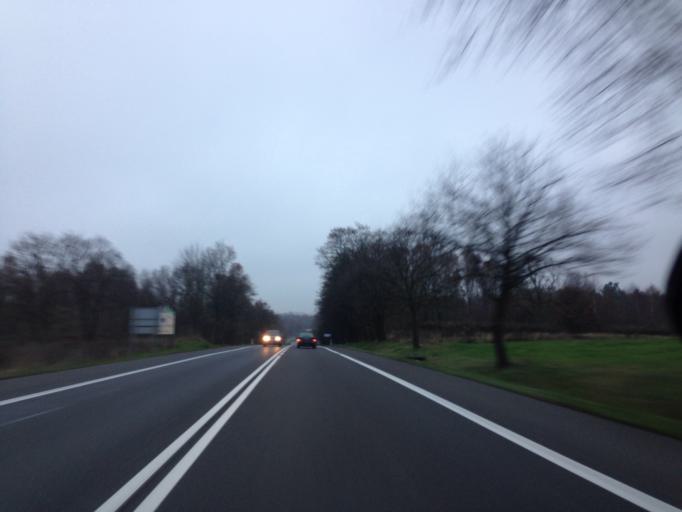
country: PL
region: Lodz Voivodeship
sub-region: Powiat zgierski
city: Strykow
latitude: 51.8475
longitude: 19.5605
